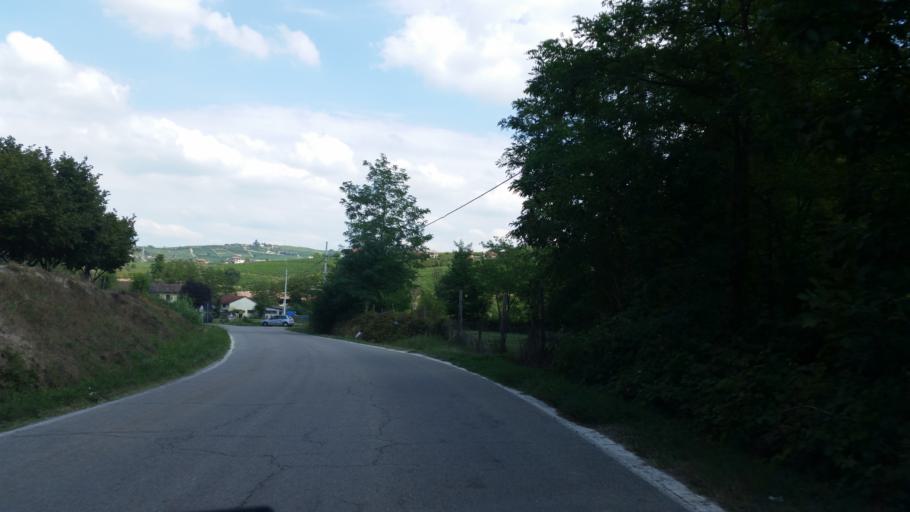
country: IT
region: Piedmont
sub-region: Provincia di Cuneo
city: Neive-Borgonovo
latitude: 44.7094
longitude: 8.1037
